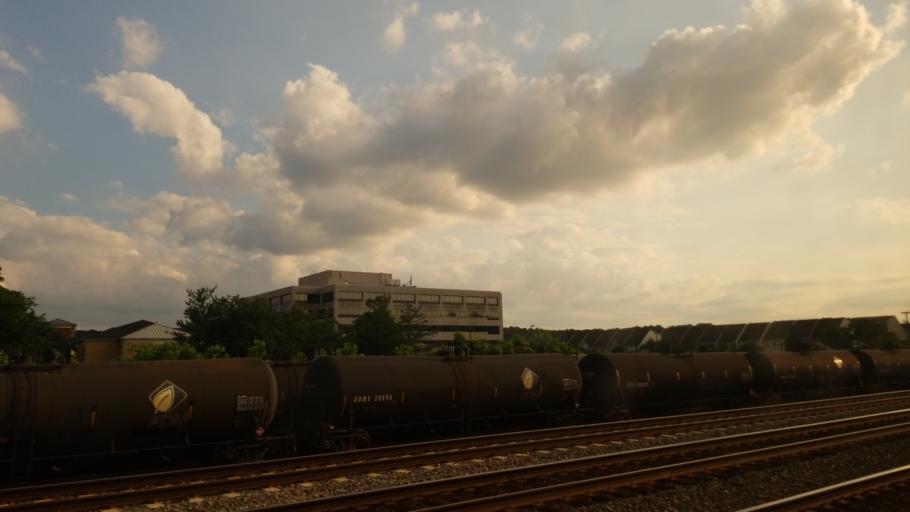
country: US
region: Virginia
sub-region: Fairfax County
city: Huntington
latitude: 38.8058
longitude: -77.0909
